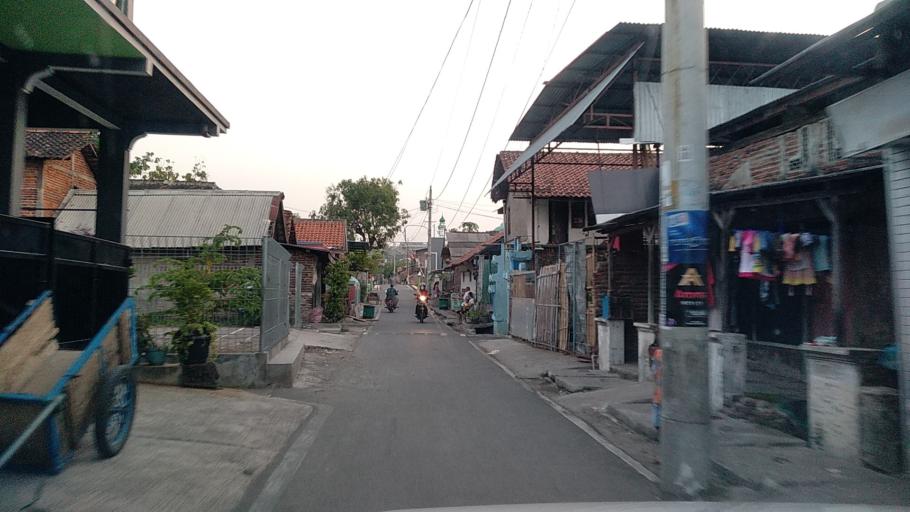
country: ID
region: Central Java
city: Semarang
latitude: -6.9730
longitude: 110.3192
